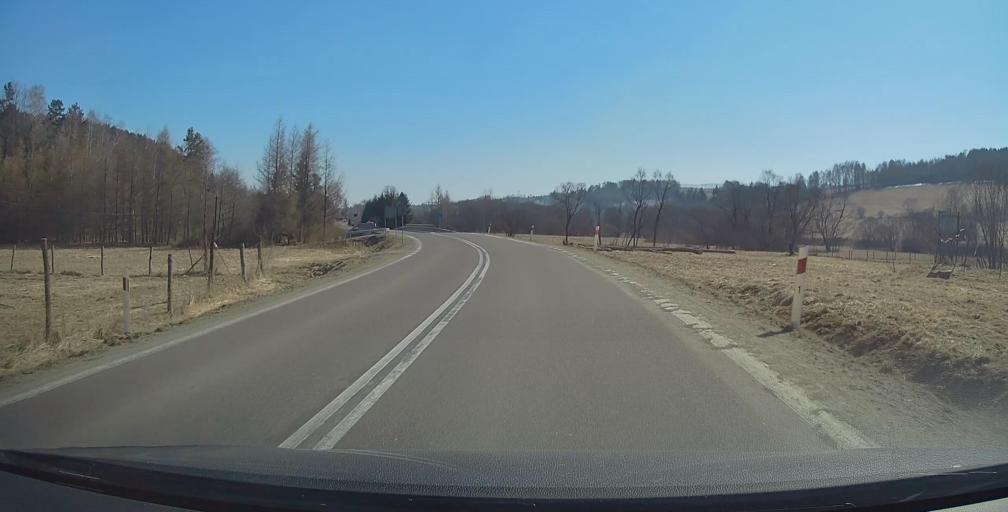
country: PL
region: Subcarpathian Voivodeship
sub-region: Powiat przemyski
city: Bircza
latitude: 49.5858
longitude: 22.5332
